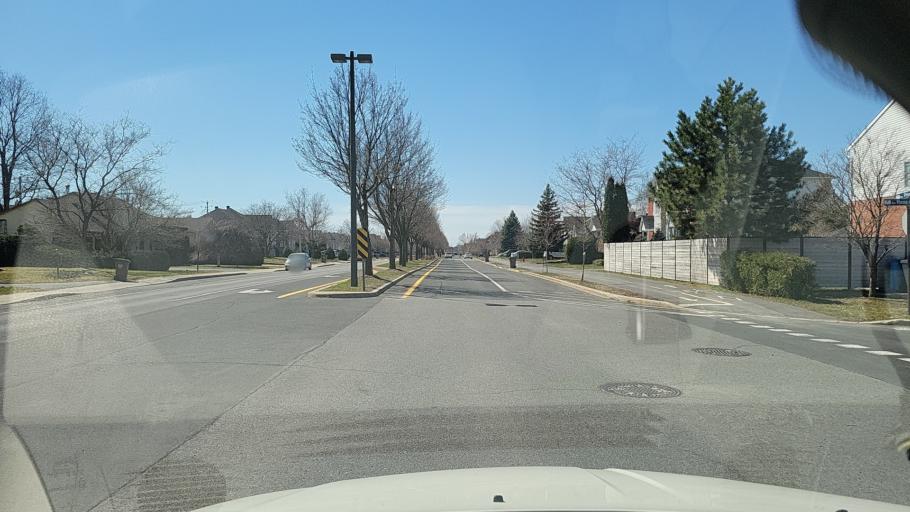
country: CA
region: Quebec
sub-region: Monteregie
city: Sainte-Julie
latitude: 45.5874
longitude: -73.3482
